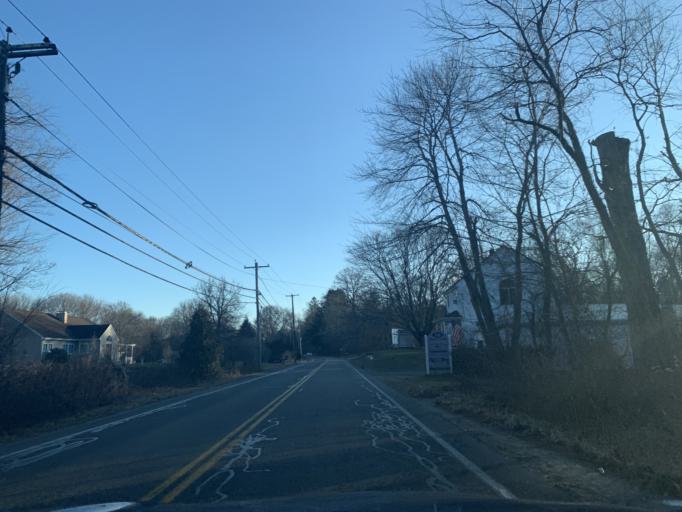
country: US
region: Massachusetts
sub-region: Bristol County
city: Rehoboth
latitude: 41.8810
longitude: -71.2302
